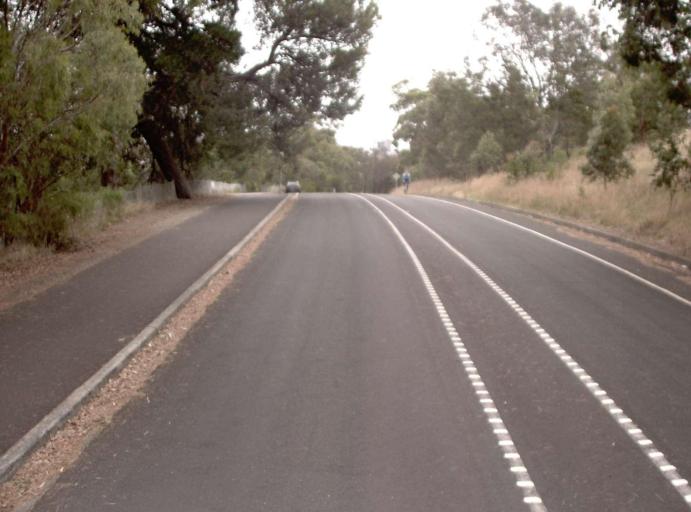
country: AU
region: Victoria
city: Abbotsford
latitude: -37.8063
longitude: 145.0031
